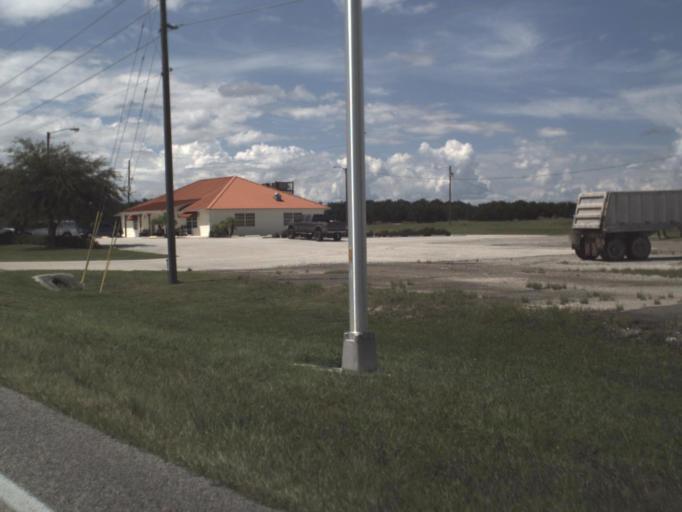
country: US
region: Florida
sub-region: Polk County
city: Babson Park
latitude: 27.8836
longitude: -81.4507
